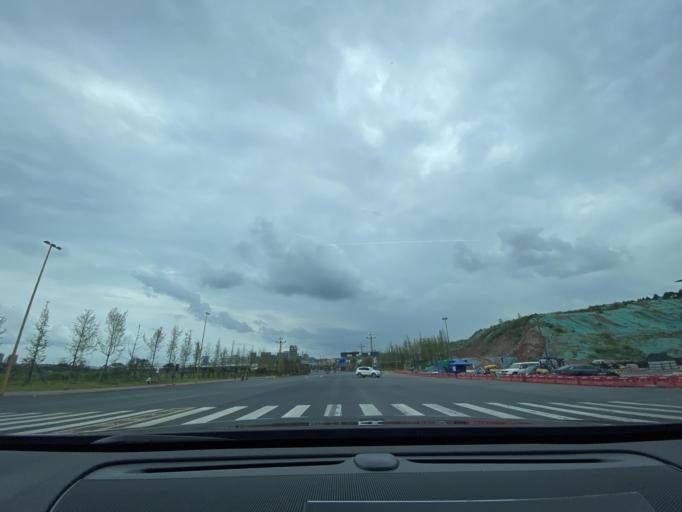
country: CN
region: Sichuan
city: Jiancheng
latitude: 30.4470
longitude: 104.4959
